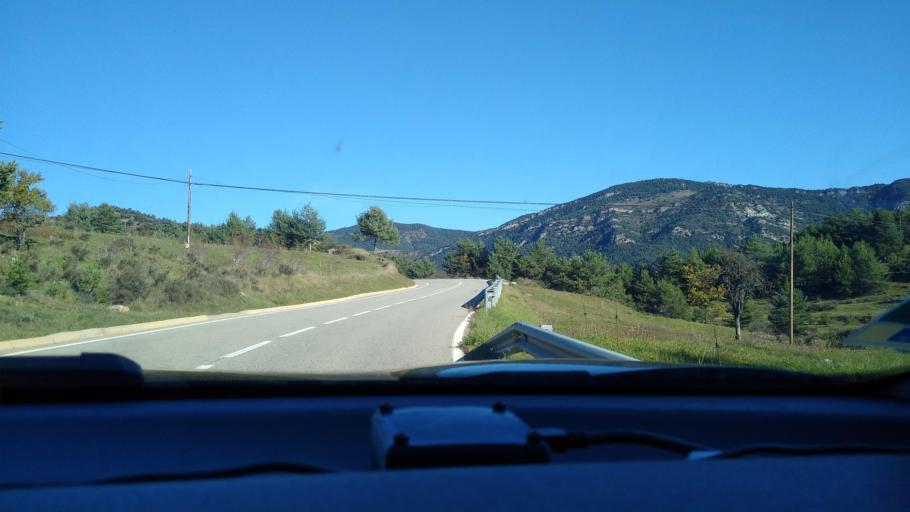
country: ES
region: Catalonia
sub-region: Provincia de Barcelona
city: Vallcebre
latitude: 42.2231
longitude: 1.8163
